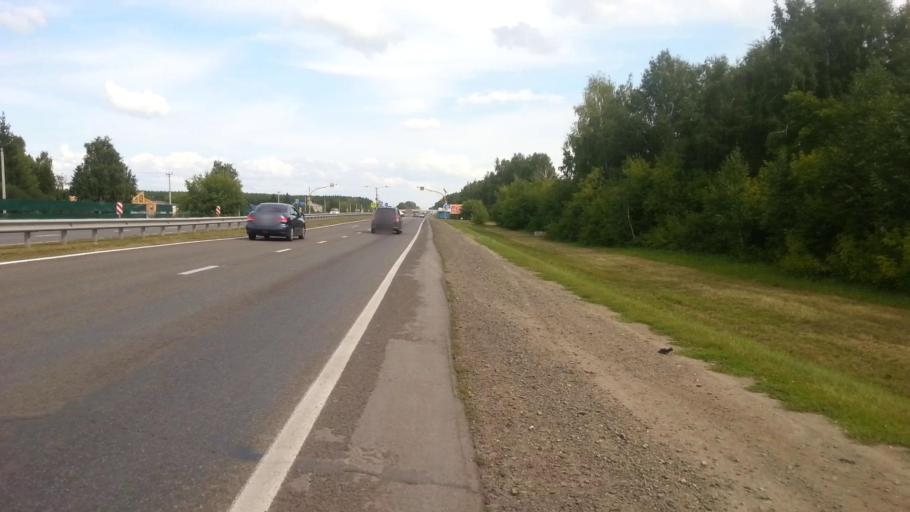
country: RU
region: Altai Krai
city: Vlasikha
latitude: 53.3545
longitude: 83.5381
